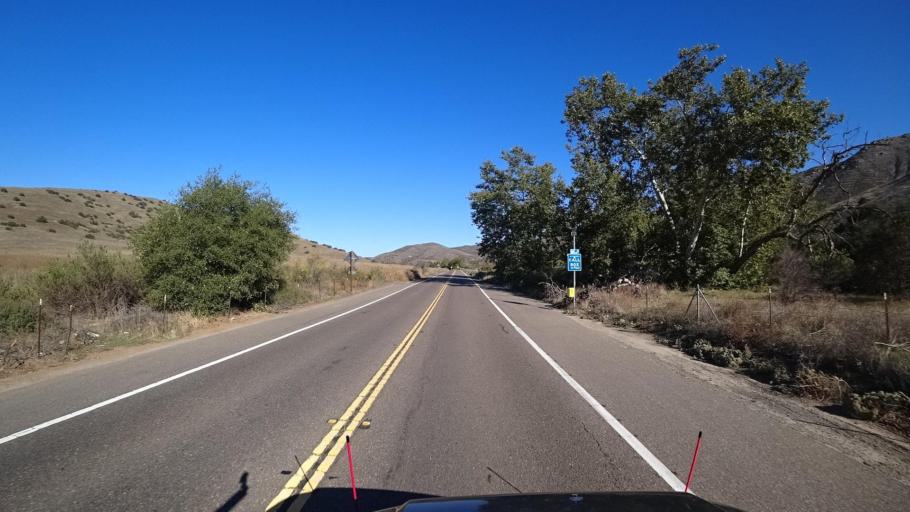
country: US
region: California
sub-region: San Diego County
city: Jamul
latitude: 32.6555
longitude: -116.8075
